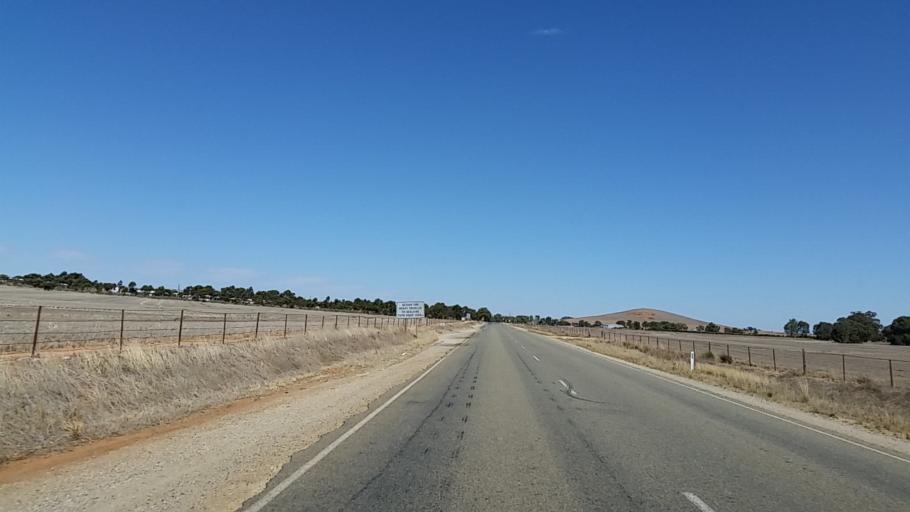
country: AU
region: South Australia
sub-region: Clare and Gilbert Valleys
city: Clare
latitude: -33.6925
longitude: 138.9075
